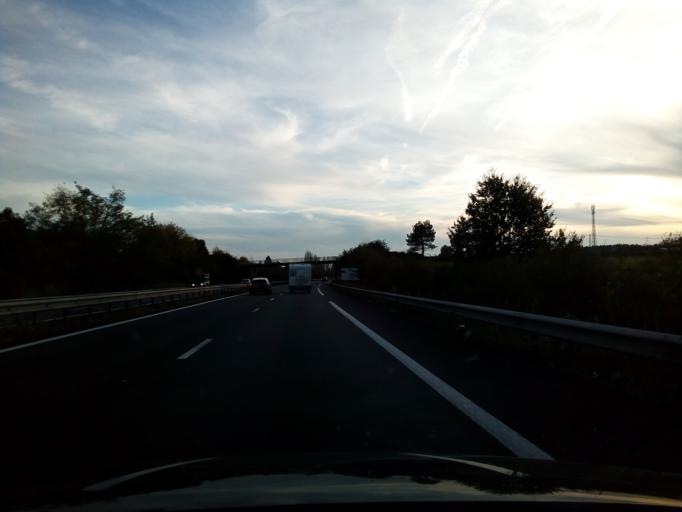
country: FR
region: Poitou-Charentes
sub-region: Departement de la Charente-Maritime
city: Montlieu-la-Garde
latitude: 45.2348
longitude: -0.2772
